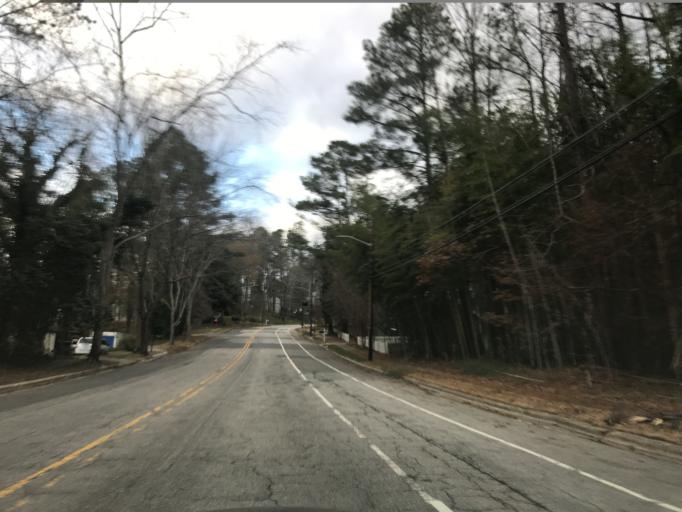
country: US
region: North Carolina
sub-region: Wake County
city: West Raleigh
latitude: 35.8485
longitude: -78.6603
